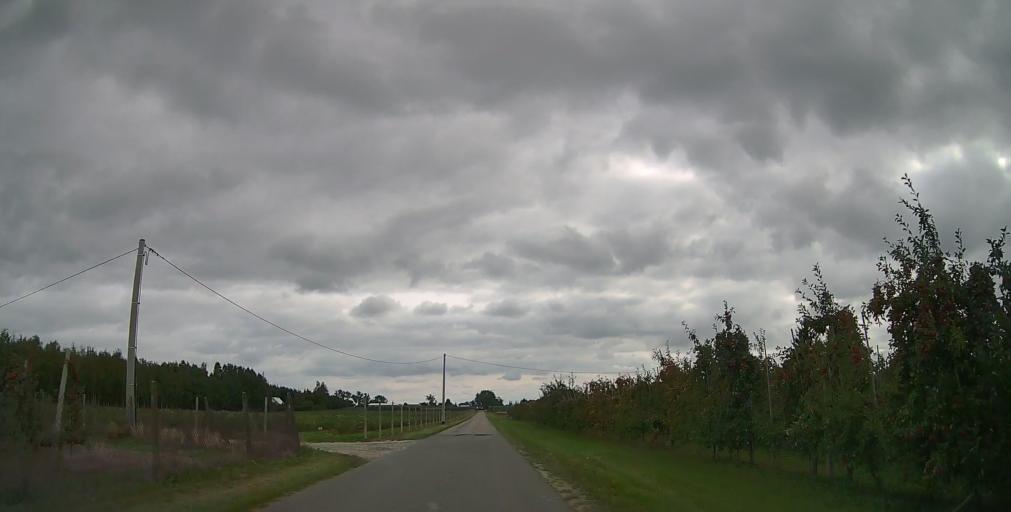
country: PL
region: Masovian Voivodeship
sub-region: Powiat grojecki
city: Goszczyn
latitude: 51.7647
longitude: 20.8689
